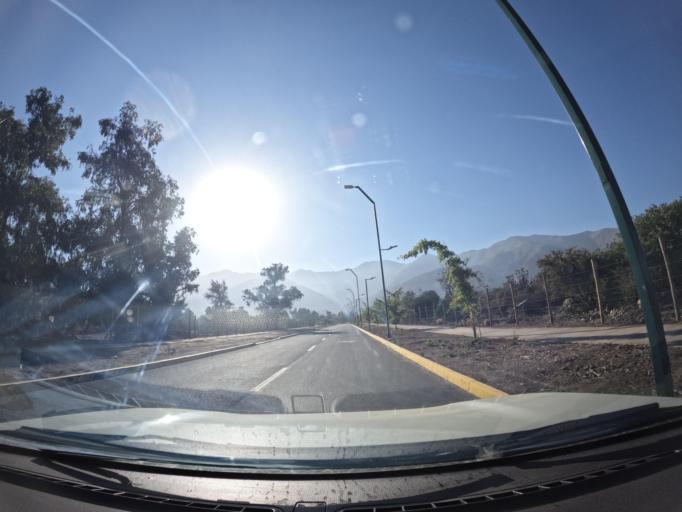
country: CL
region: Santiago Metropolitan
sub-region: Provincia de Santiago
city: Villa Presidente Frei, Nunoa, Santiago, Chile
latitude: -33.5021
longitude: -70.5389
